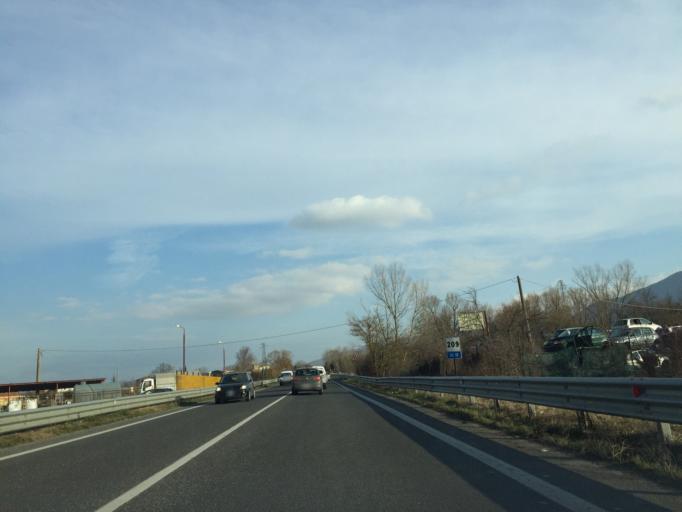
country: IT
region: Molise
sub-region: Provincia di Campobasso
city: San Polomatese
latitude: 41.4819
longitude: 14.4966
